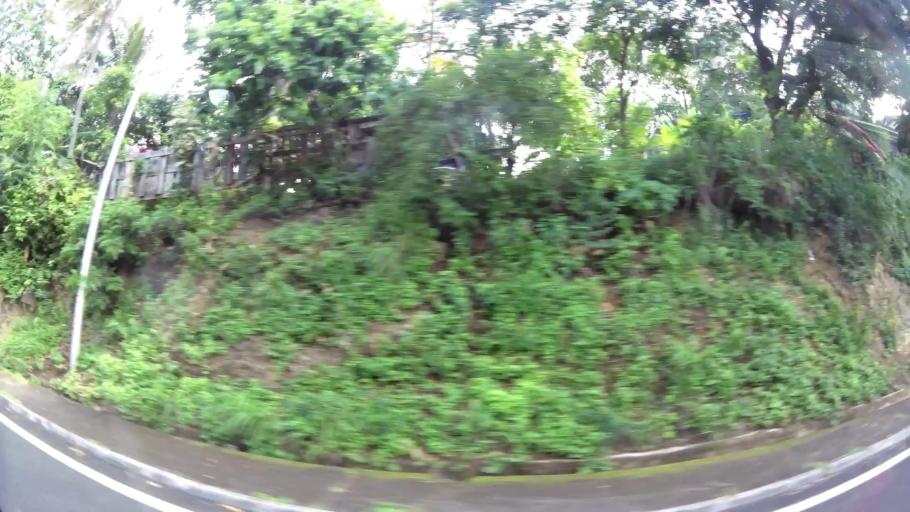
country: GP
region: Guadeloupe
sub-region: Guadeloupe
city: Basse-Terre
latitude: 16.0017
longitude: -61.7217
